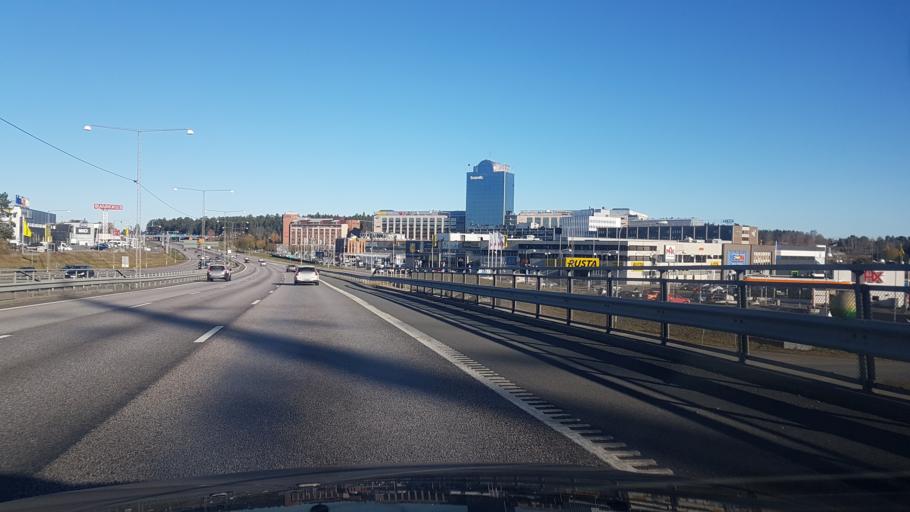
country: SE
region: Stockholm
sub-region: Upplands Vasby Kommun
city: Upplands Vaesby
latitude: 59.4954
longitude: 17.9228
